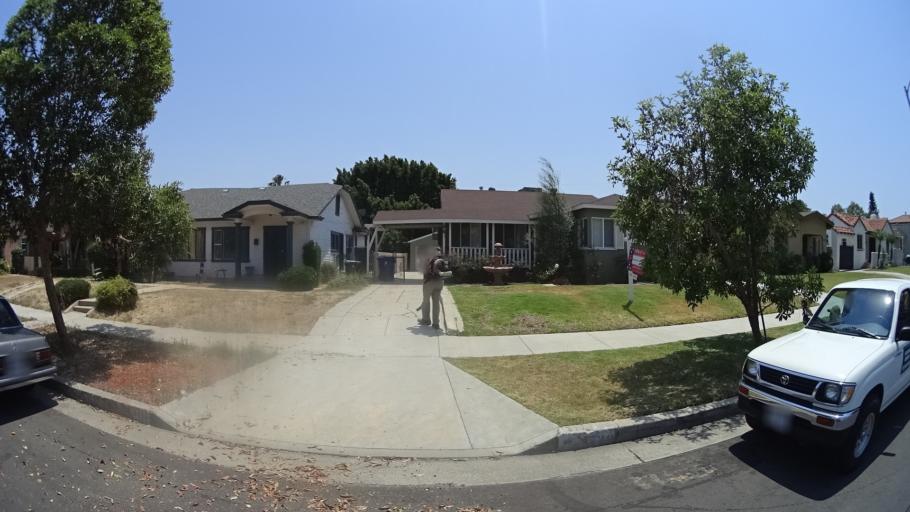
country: US
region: California
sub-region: Los Angeles County
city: View Park-Windsor Hills
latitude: 33.9881
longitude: -118.3386
